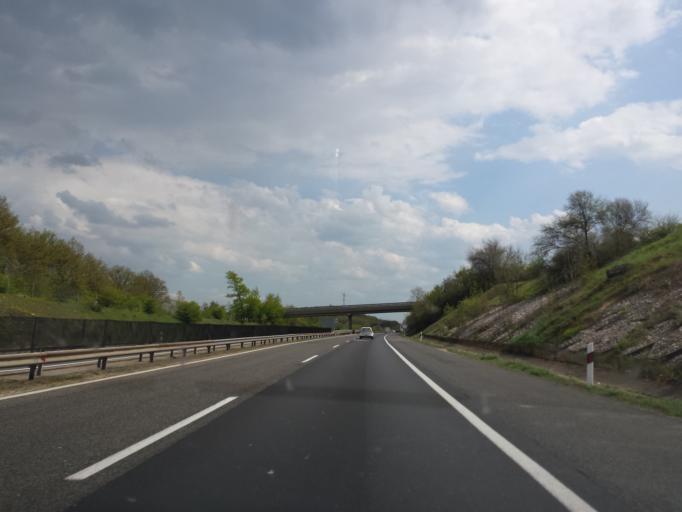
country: HU
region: Fejer
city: Szarliget
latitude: 47.5155
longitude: 18.5316
